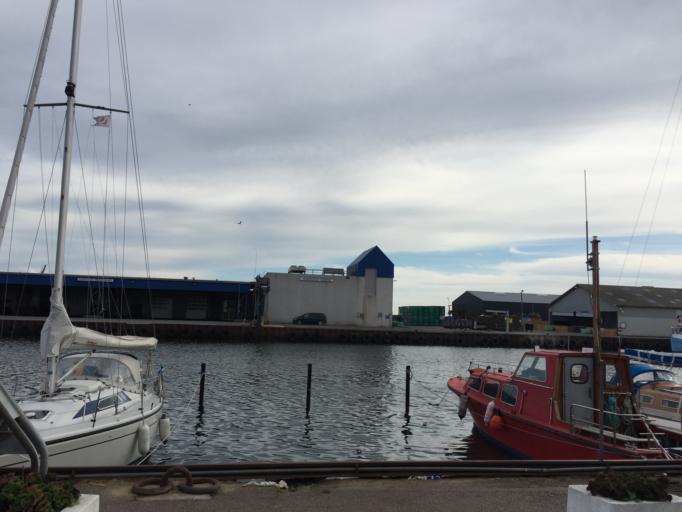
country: DK
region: Capital Region
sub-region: Halsnaes Kommune
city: Hundested
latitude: 55.9639
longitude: 11.8473
